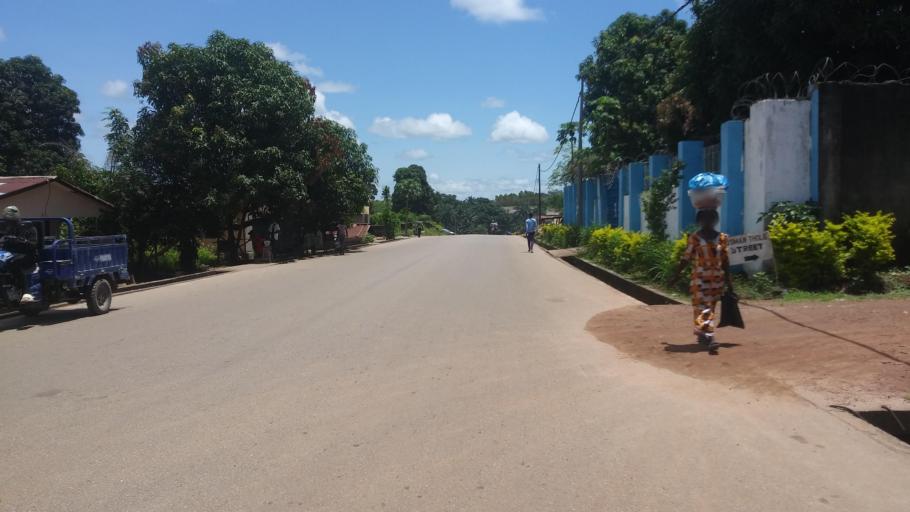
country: SL
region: Northern Province
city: Makeni
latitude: 8.8793
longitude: -12.0314
